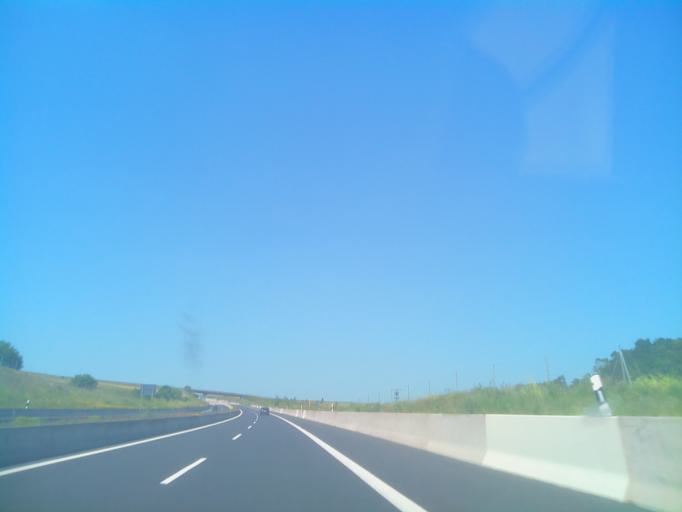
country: DE
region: Bavaria
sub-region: Regierungsbezirk Unterfranken
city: Hollstadt
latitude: 50.3497
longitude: 10.3157
